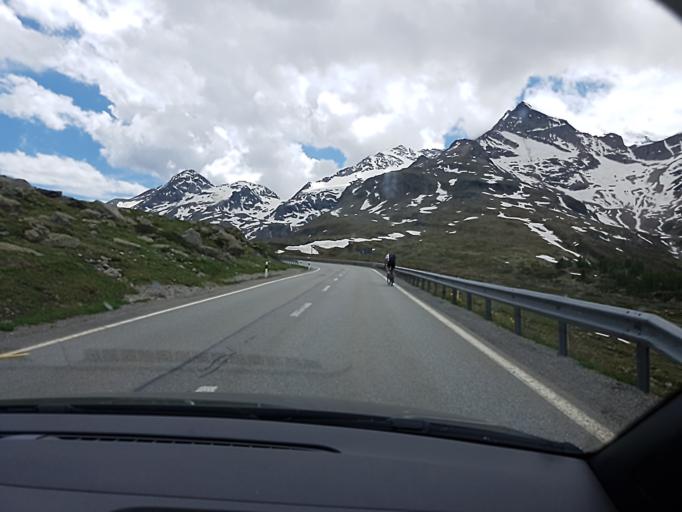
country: CH
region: Grisons
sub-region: Bernina District
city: Poschiavo
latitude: 46.4275
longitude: 9.9992
